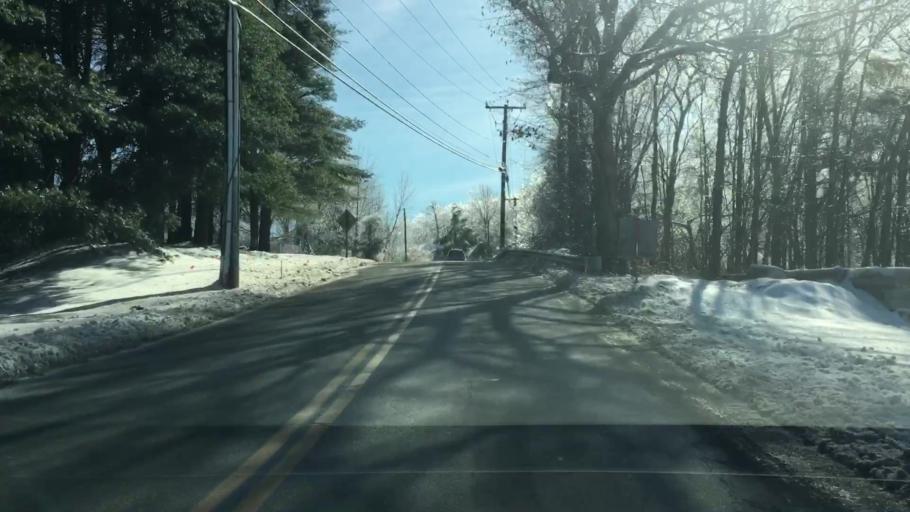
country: US
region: Connecticut
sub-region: Fairfield County
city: Newtown
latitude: 41.4064
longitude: -73.2633
